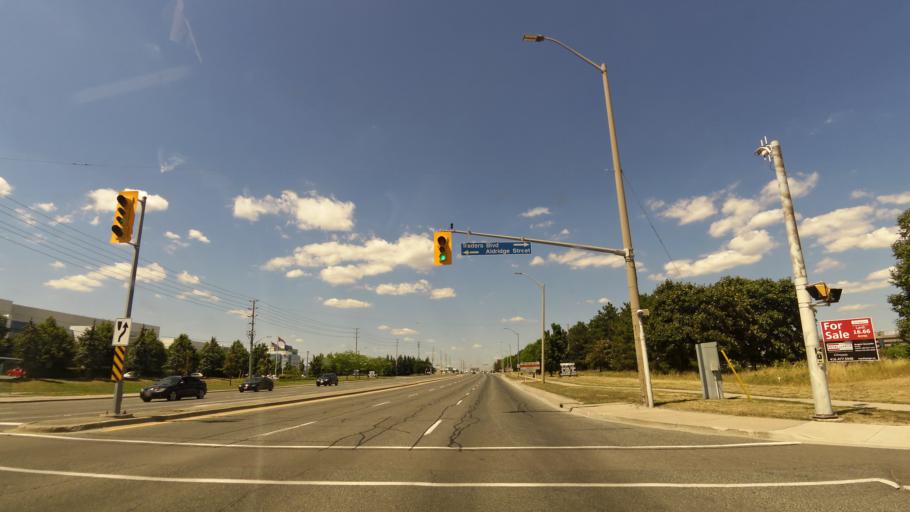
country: CA
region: Ontario
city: Mississauga
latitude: 43.6231
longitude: -79.6748
